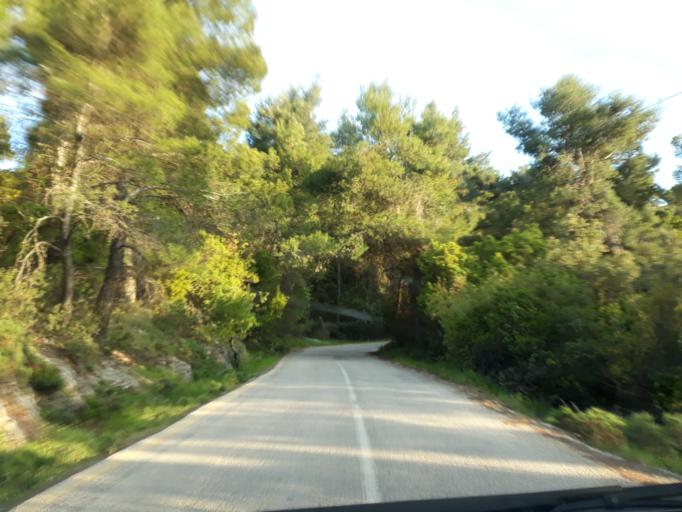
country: GR
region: Attica
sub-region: Nomarchia Anatolikis Attikis
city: Afidnes
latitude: 38.2207
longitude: 23.7804
